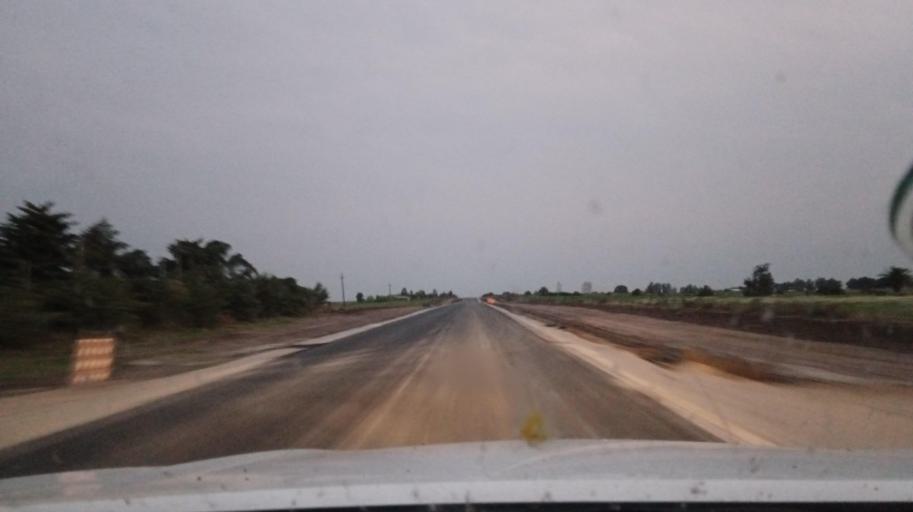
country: UY
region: Canelones
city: Sauce
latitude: -34.5769
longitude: -56.1010
